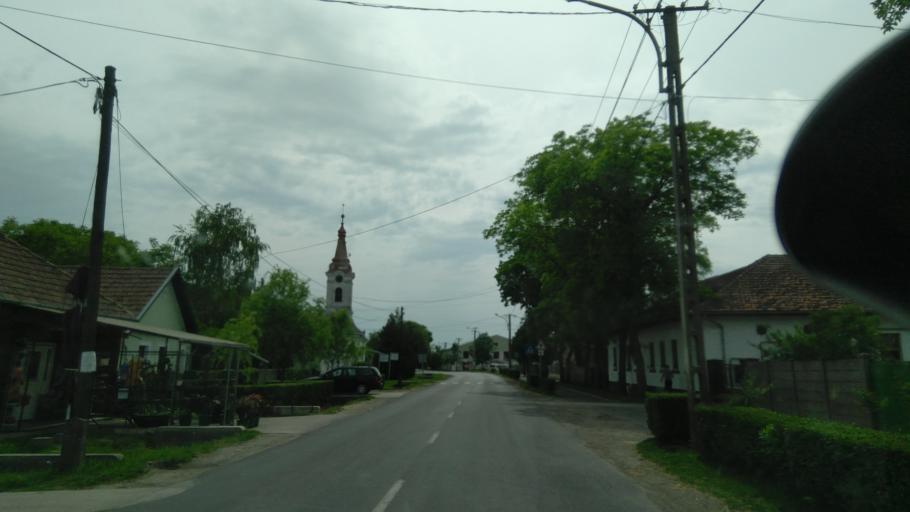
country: HU
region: Bekes
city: Sarkad
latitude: 46.8106
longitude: 21.3827
